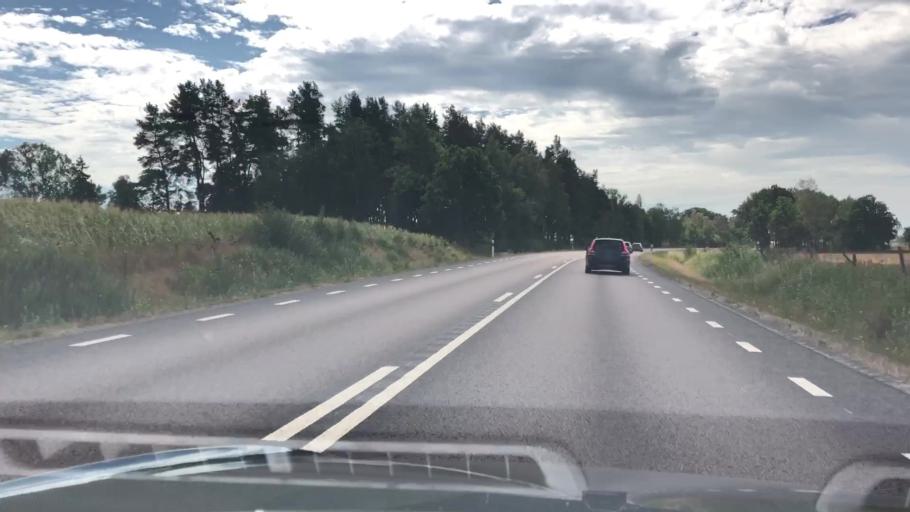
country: SE
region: Kalmar
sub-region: Torsas Kommun
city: Torsas
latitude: 56.3611
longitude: 16.0623
